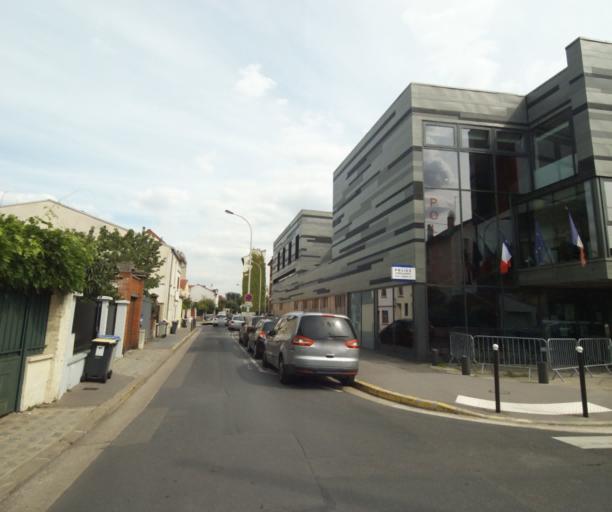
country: FR
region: Ile-de-France
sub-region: Departement des Hauts-de-Seine
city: Bois-Colombes
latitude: 48.9204
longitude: 2.2736
